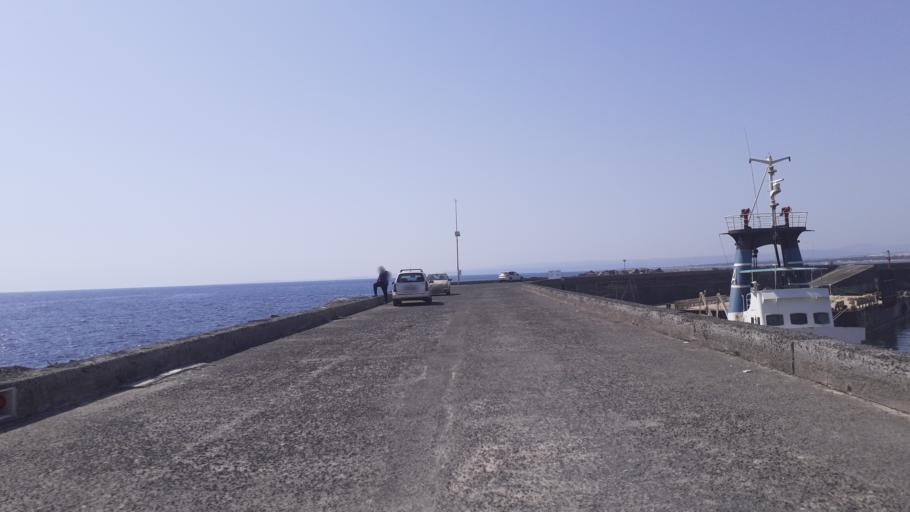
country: IT
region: Sicily
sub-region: Catania
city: Catania
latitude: 37.4890
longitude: 15.1001
